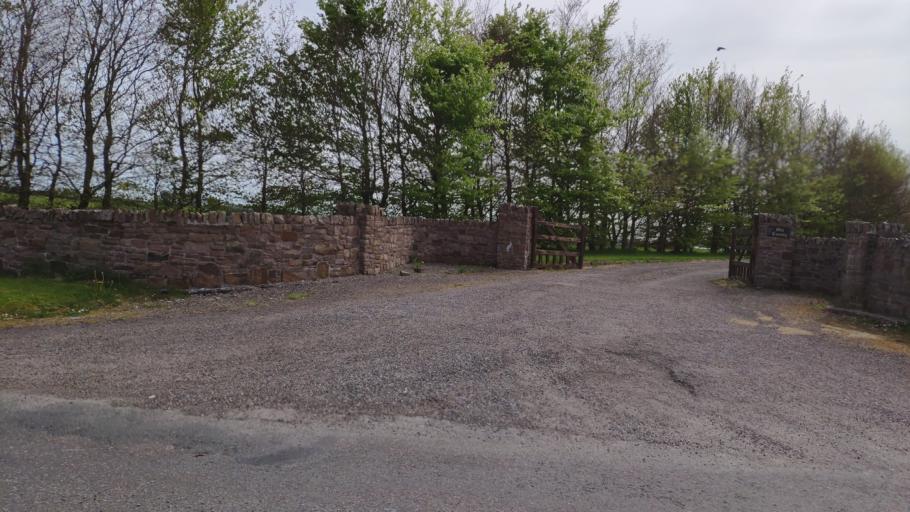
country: IE
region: Munster
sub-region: County Cork
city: Blarney
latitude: 51.9882
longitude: -8.5083
